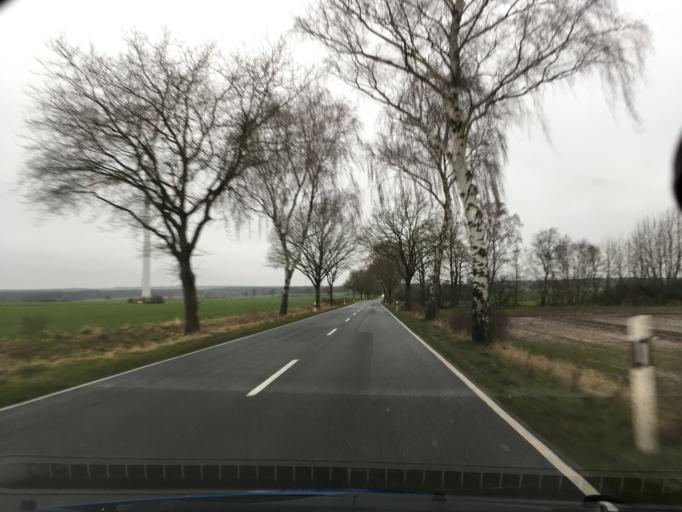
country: DE
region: Lower Saxony
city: Reinstorf
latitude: 53.2634
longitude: 10.5794
